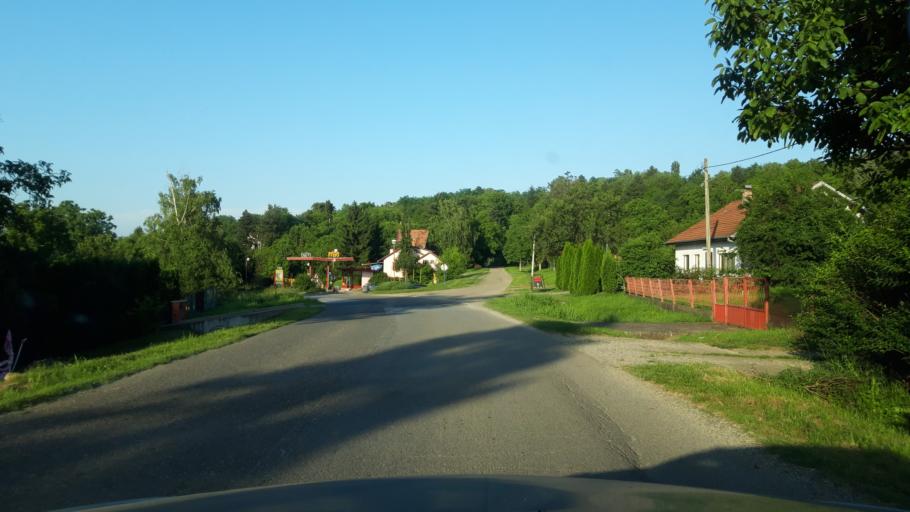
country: RS
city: Glozan
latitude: 45.2157
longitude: 19.6266
